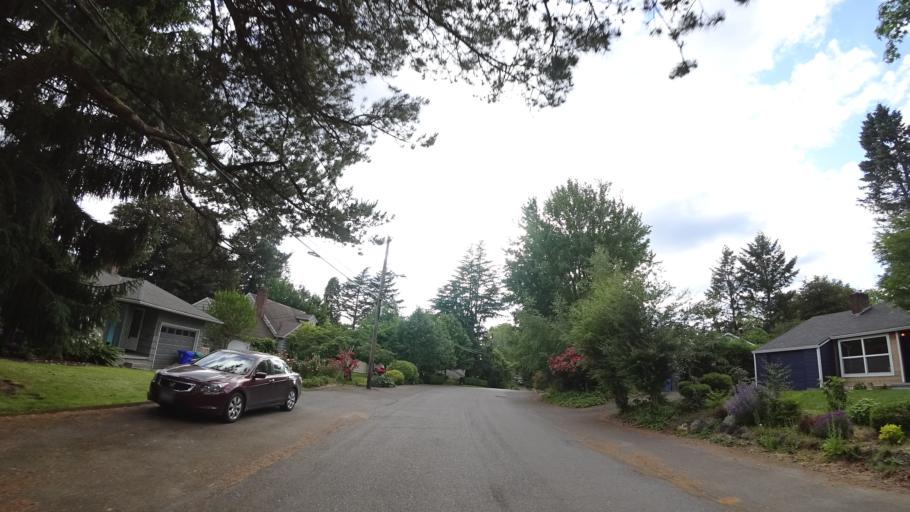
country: US
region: Oregon
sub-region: Washington County
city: Raleigh Hills
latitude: 45.4781
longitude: -122.7339
